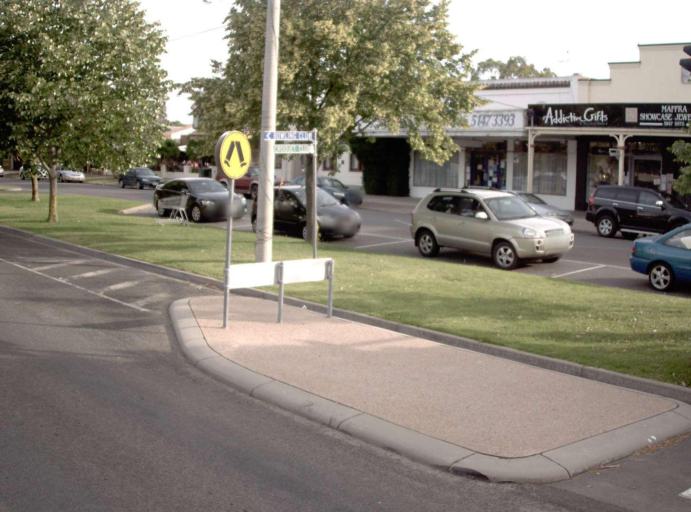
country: AU
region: Victoria
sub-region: Wellington
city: Sale
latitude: -37.9669
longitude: 146.9761
